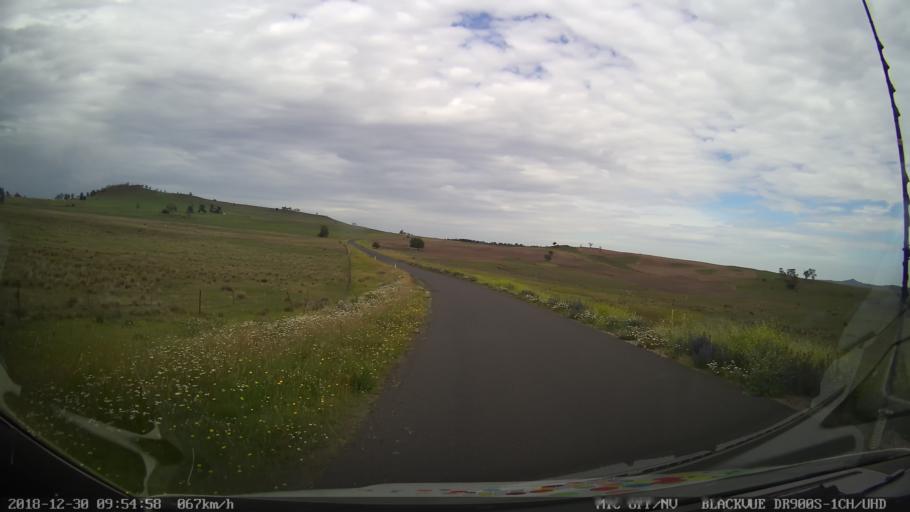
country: AU
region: New South Wales
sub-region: Cooma-Monaro
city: Cooma
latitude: -36.5189
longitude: 149.2709
